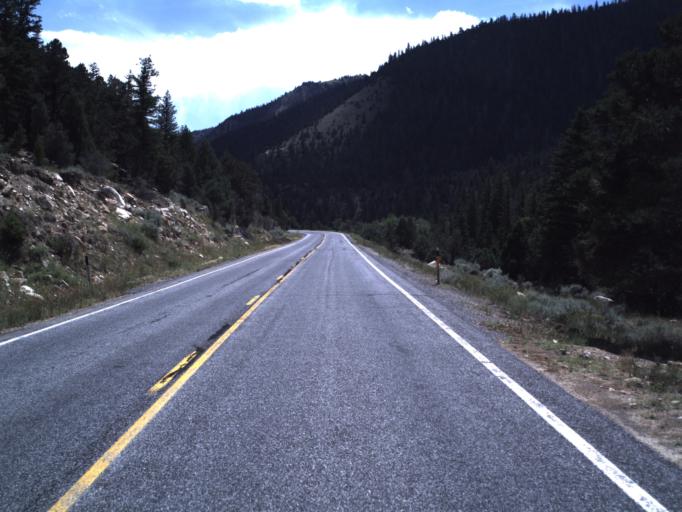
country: US
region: Utah
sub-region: Emery County
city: Huntington
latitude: 39.4297
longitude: -111.1300
